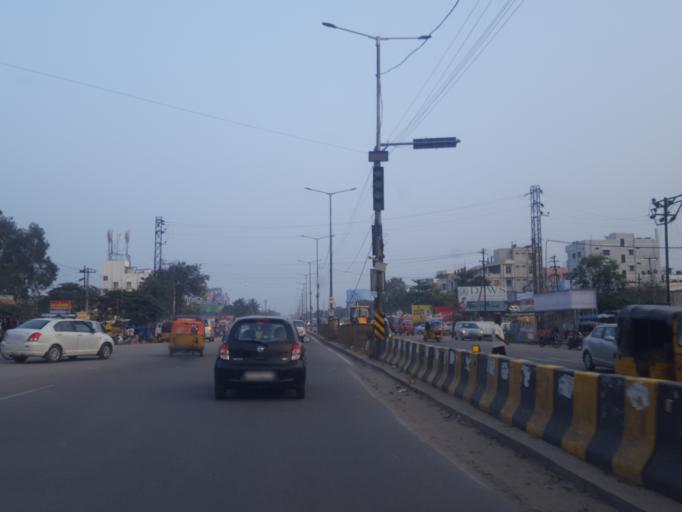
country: IN
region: Telangana
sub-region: Medak
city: Serilingampalle
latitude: 17.5092
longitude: 78.3003
